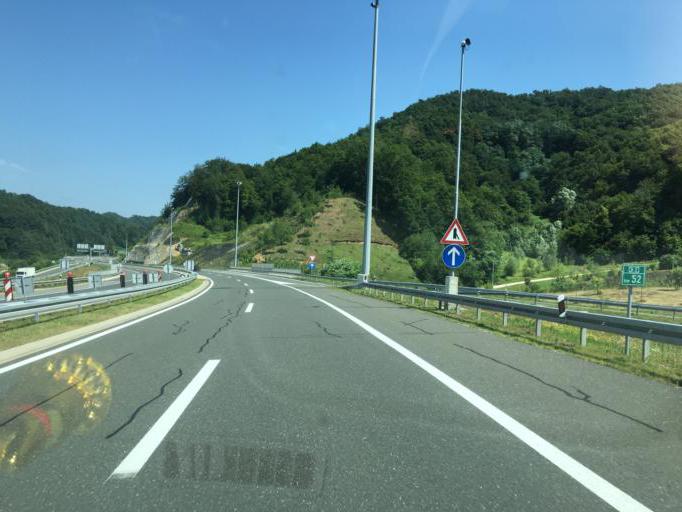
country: HR
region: Krapinsko-Zagorska
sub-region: Grad Krapina
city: Krapina
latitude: 46.2009
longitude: 15.8454
